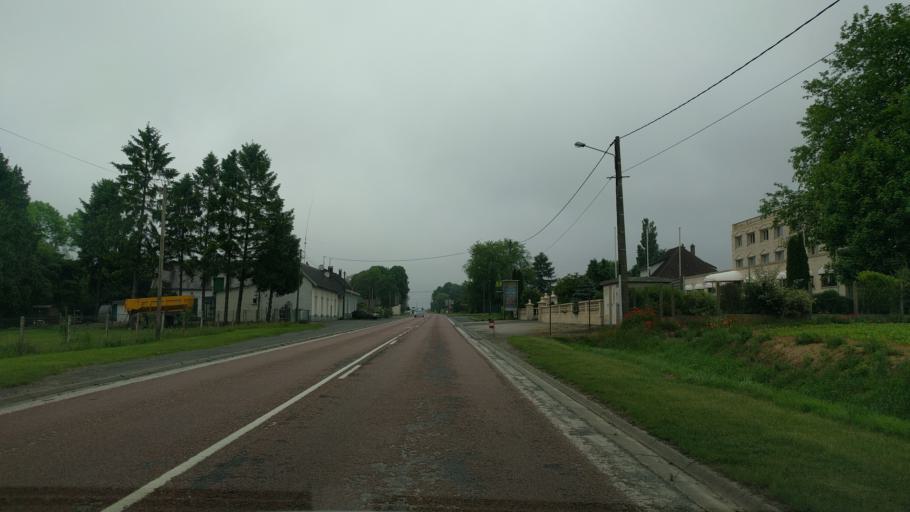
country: FR
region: Picardie
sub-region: Departement de la Somme
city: Moislains
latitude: 50.0024
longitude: 2.9099
